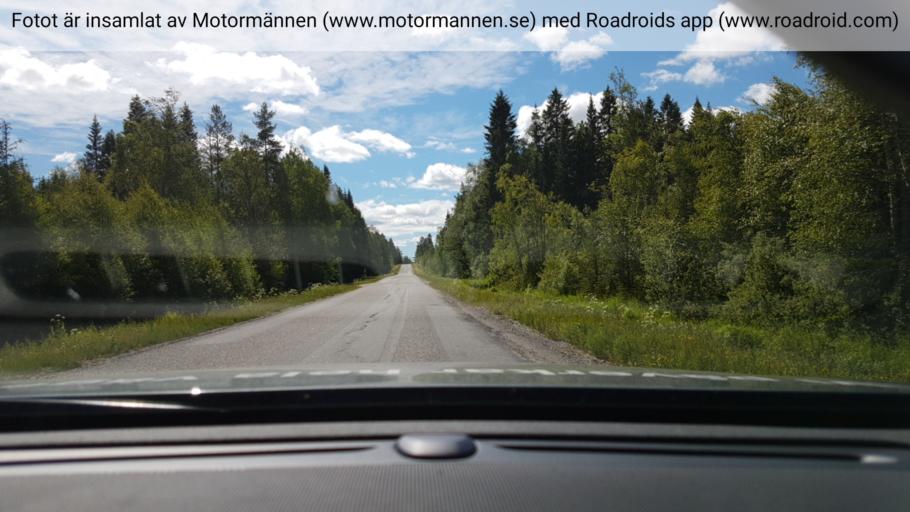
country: SE
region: Vaesterbotten
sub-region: Skelleftea Kommun
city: Burea
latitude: 64.4286
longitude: 21.3534
